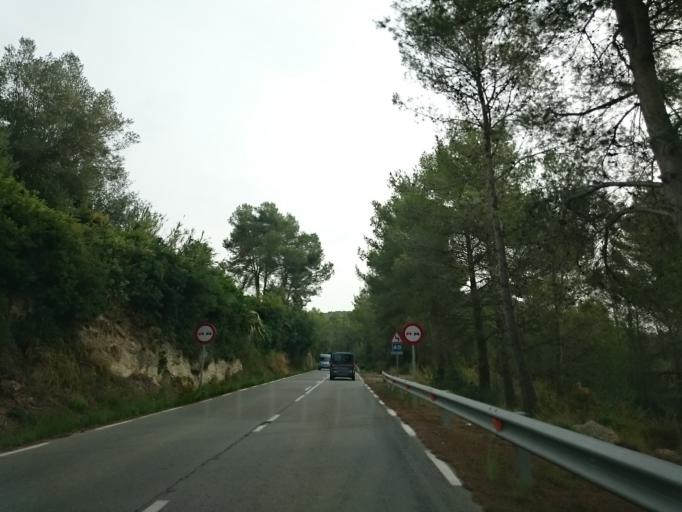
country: ES
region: Catalonia
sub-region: Provincia de Barcelona
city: Sant Pere de Ribes
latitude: 41.2939
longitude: 1.7801
